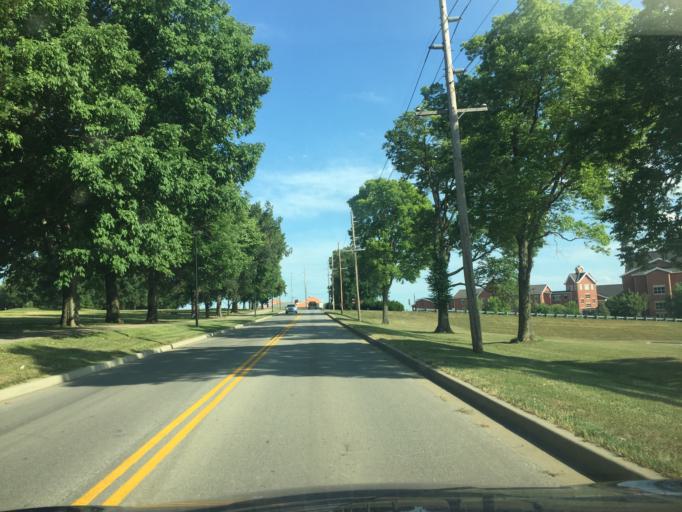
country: US
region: Kansas
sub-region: Leavenworth County
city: Leavenworth
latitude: 39.3453
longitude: -94.9280
